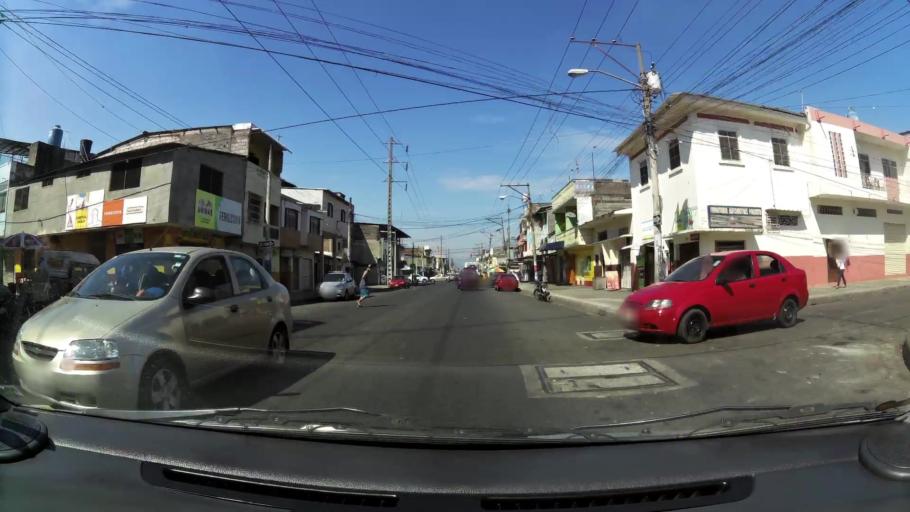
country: EC
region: Guayas
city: Guayaquil
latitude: -2.2098
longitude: -79.9130
